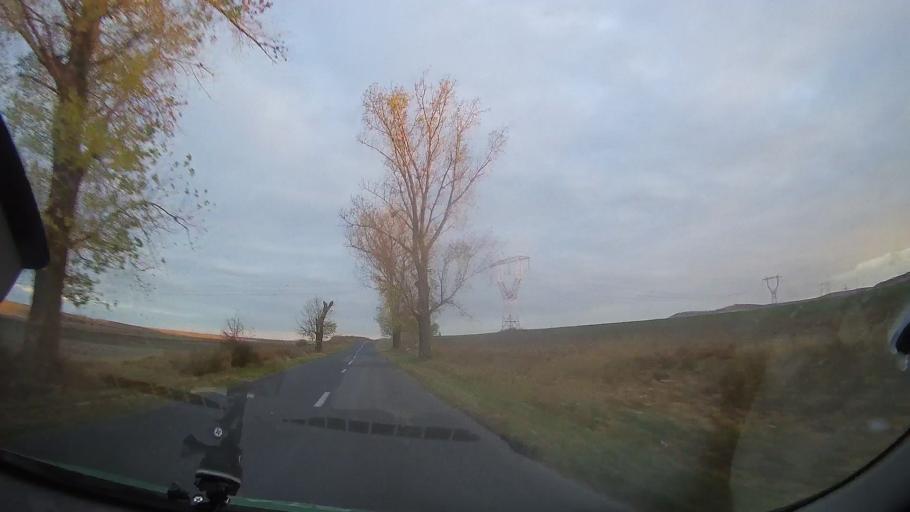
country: RO
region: Tulcea
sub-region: Comuna Mihai Bravu
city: Turda
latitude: 44.9873
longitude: 28.6091
